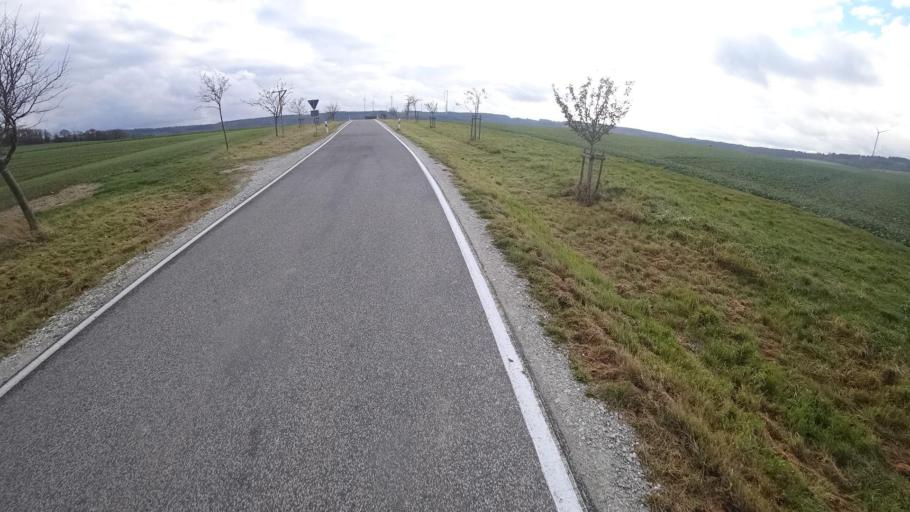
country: DE
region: Rheinland-Pfalz
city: Utzenhain
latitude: 50.1266
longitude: 7.6337
